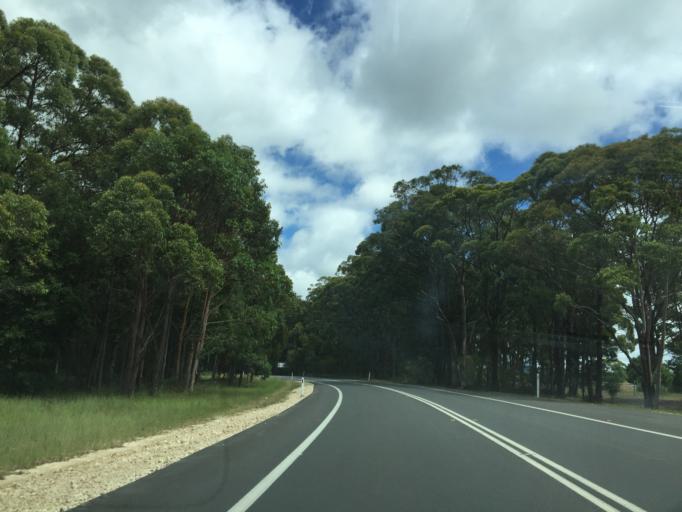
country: AU
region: New South Wales
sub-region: Hawkesbury
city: Richmond
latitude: -33.5098
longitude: 150.5677
